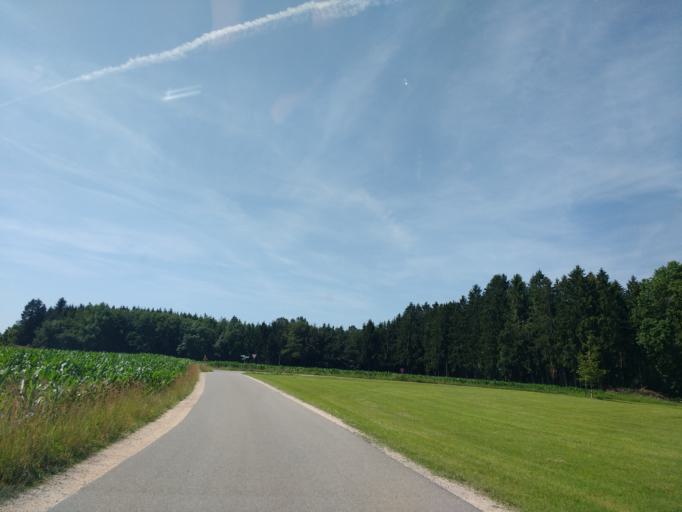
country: DE
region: Bavaria
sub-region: Upper Bavaria
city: Seeon-Seebruck
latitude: 47.9917
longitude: 12.4483
